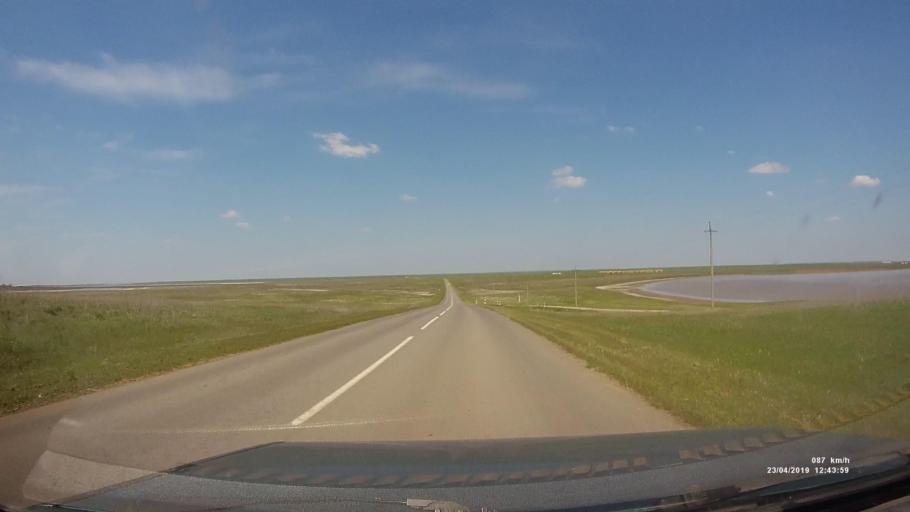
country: RU
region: Kalmykiya
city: Yashalta
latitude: 46.4710
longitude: 42.6497
